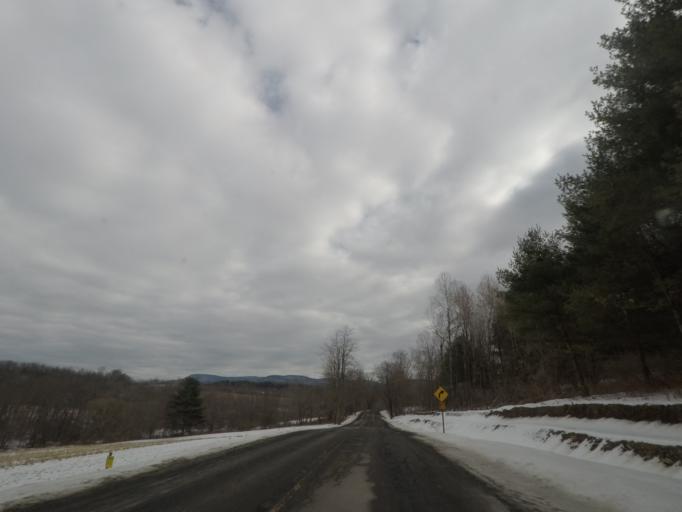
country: US
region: New York
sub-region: Rensselaer County
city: Hoosick Falls
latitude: 42.8625
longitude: -73.3595
